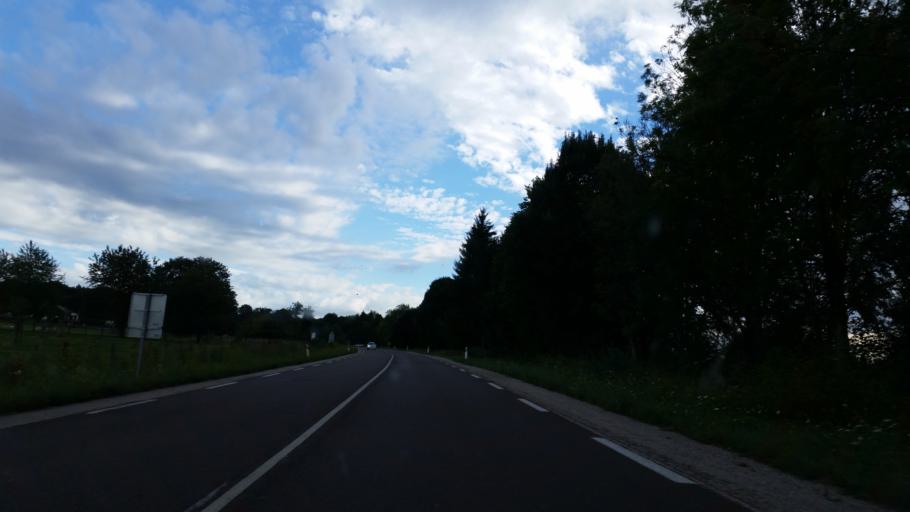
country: FR
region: Franche-Comte
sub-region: Departement de la Haute-Saone
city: Fougerolles
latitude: 47.8788
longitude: 6.3830
